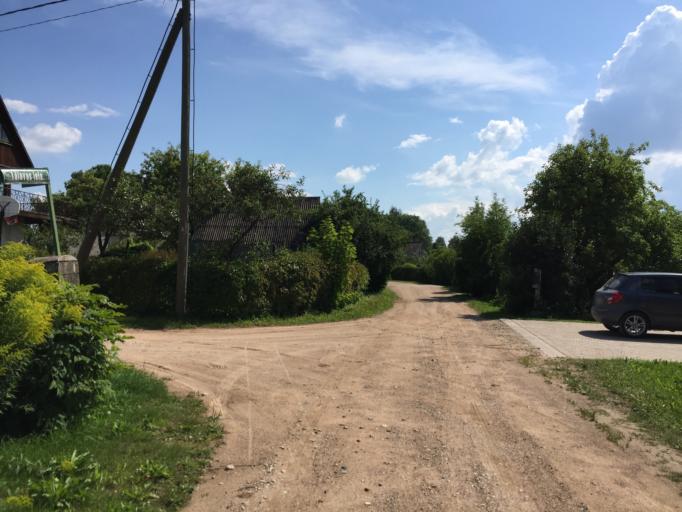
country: LV
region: Sigulda
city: Sigulda
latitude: 57.1454
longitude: 24.8399
